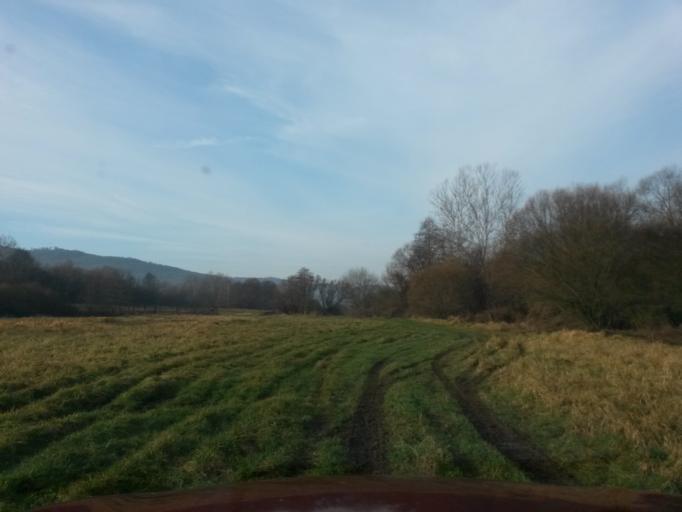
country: SK
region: Kosicky
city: Roznava
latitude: 48.7120
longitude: 20.4530
